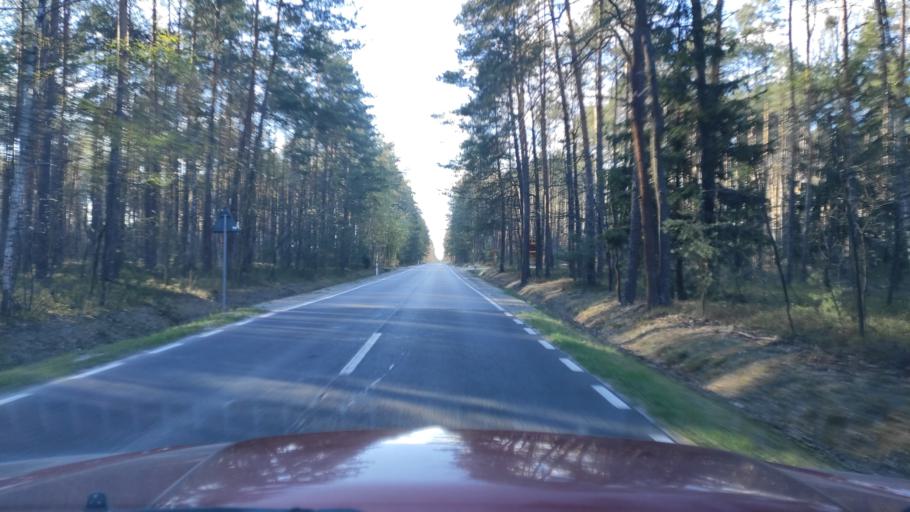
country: PL
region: Masovian Voivodeship
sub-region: Powiat zwolenski
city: Zwolen
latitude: 51.3890
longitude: 21.5511
